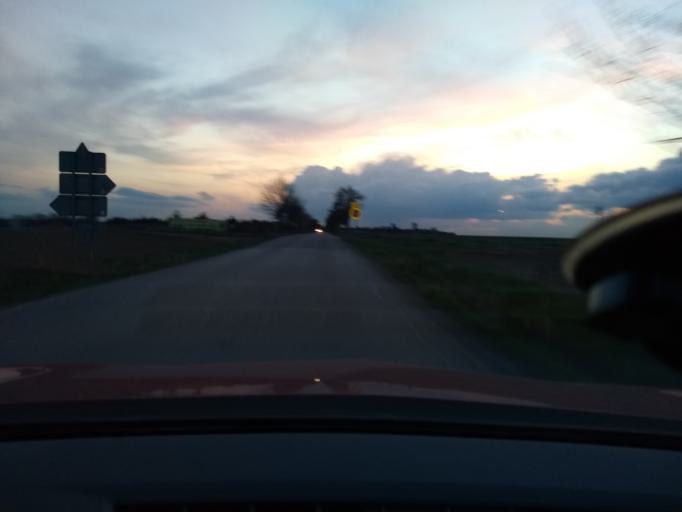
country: CZ
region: Central Bohemia
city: Jenec
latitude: 50.0690
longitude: 14.2230
